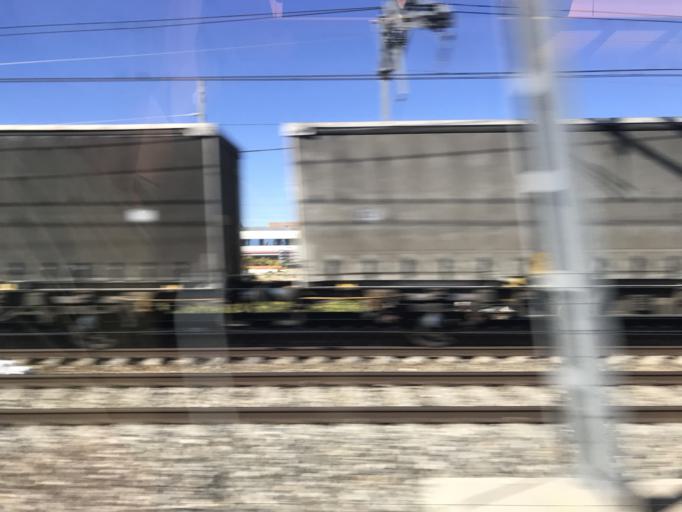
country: ES
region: Madrid
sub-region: Provincia de Madrid
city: Las Tablas
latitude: 40.4983
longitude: -3.6790
